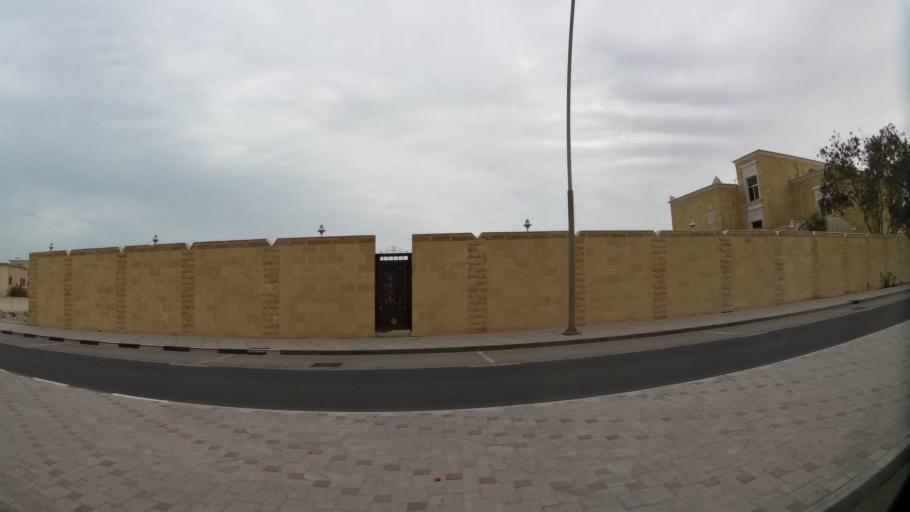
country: QA
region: Baladiyat ad Dawhah
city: Doha
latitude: 25.3444
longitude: 51.4925
